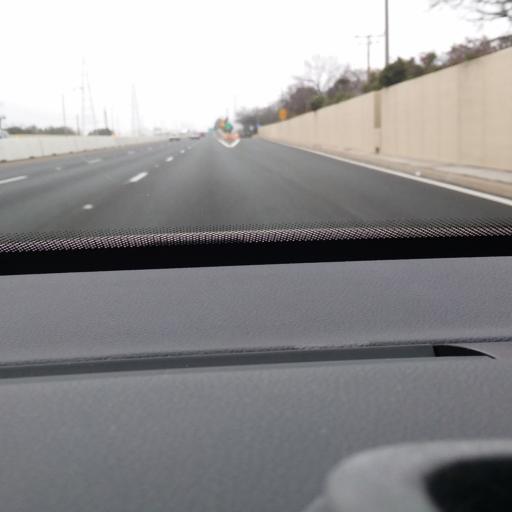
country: US
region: Texas
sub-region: Dallas County
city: University Park
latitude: 32.8980
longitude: -96.8093
